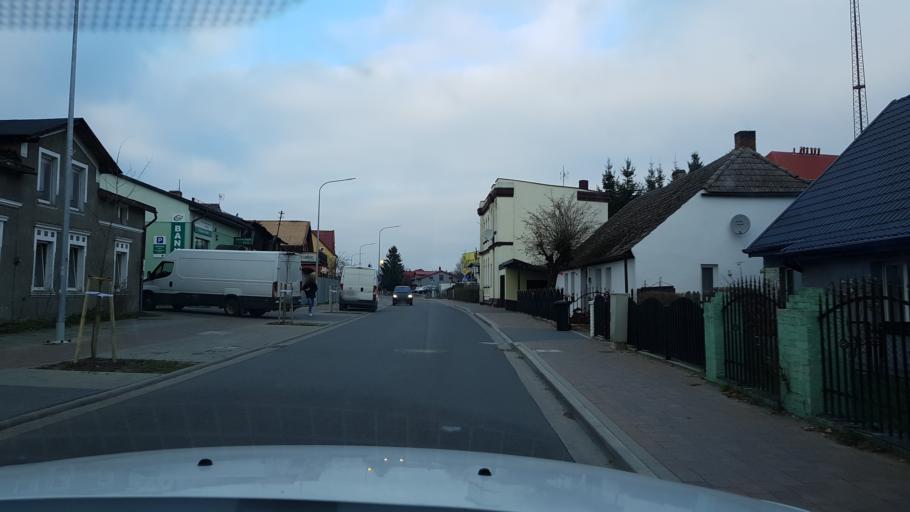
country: PL
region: West Pomeranian Voivodeship
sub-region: Powiat kolobrzeski
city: Goscino
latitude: 54.0490
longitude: 15.6547
